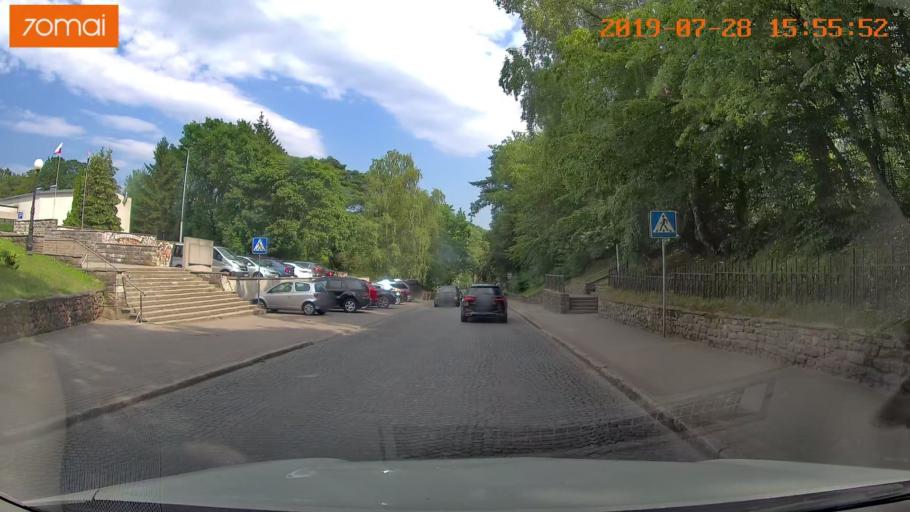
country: RU
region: Kaliningrad
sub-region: Gorod Svetlogorsk
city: Svetlogorsk
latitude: 54.9405
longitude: 20.1425
